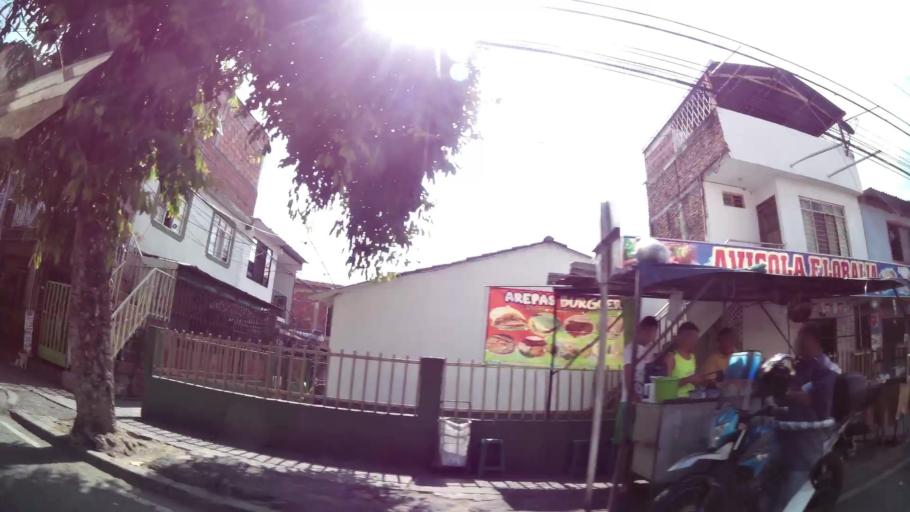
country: CO
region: Valle del Cauca
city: Cali
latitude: 3.4971
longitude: -76.4895
